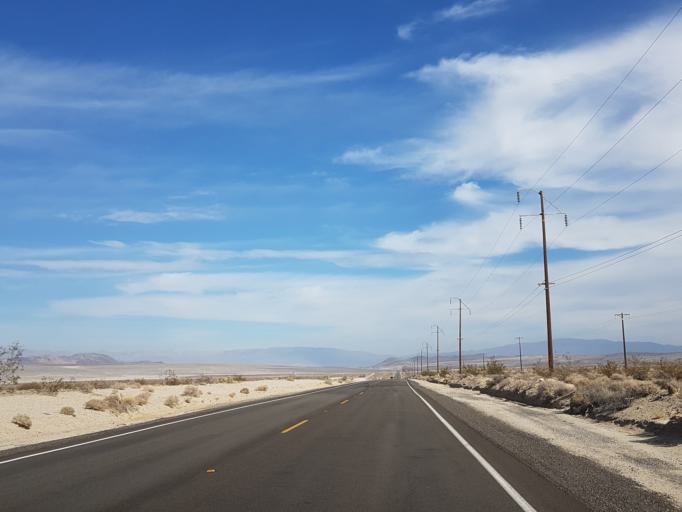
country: US
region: California
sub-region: Kern County
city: Ridgecrest
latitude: 35.6438
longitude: -117.5387
